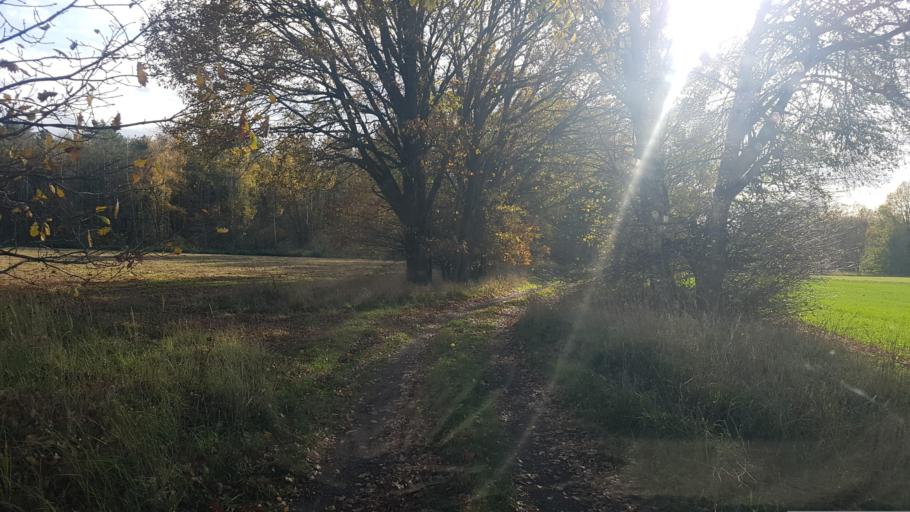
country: DE
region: Brandenburg
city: Wiesenburg
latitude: 52.0764
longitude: 12.4640
